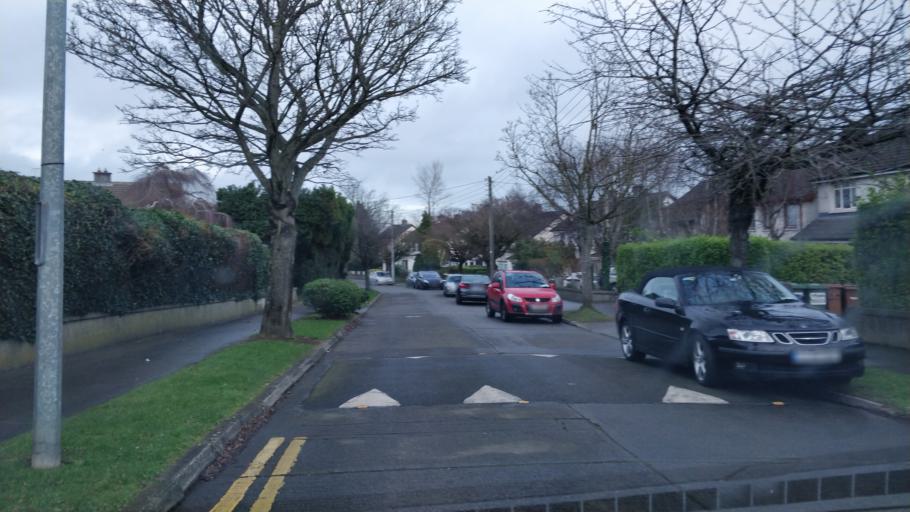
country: IE
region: Leinster
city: Foxrock
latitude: 53.2800
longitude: -6.1731
